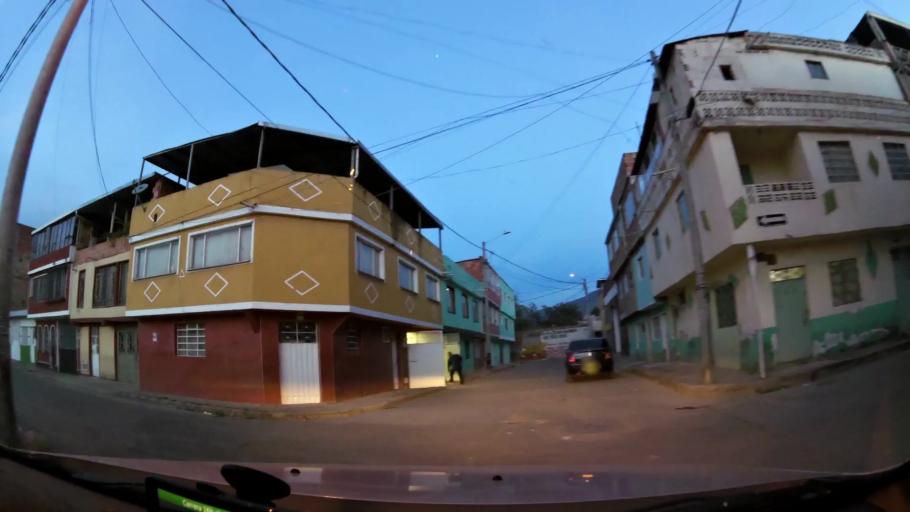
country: CO
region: Bogota D.C.
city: Bogota
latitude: 4.5528
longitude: -74.1355
